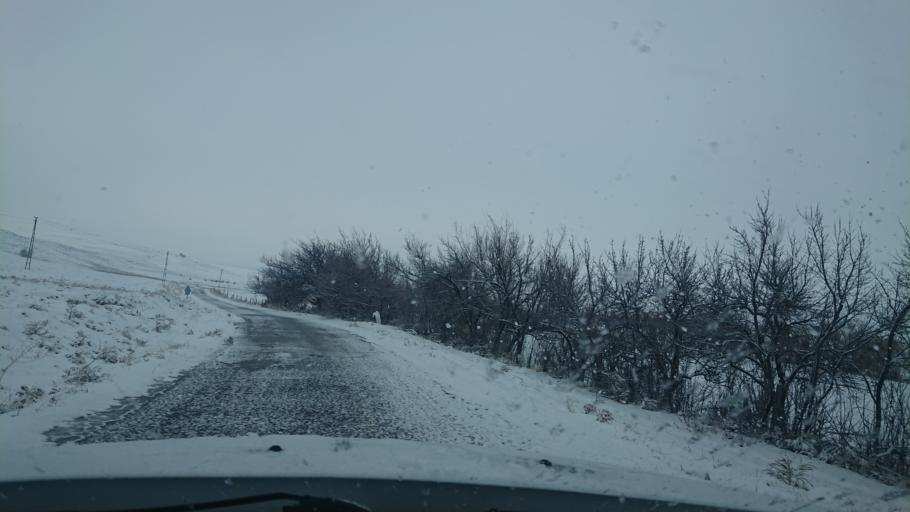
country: TR
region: Aksaray
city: Acipinar
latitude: 38.6779
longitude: 33.8668
